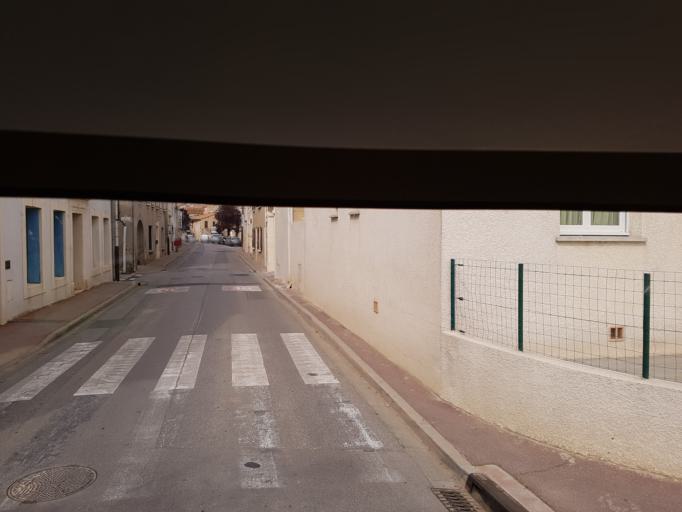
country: FR
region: Languedoc-Roussillon
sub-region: Departement de l'Aude
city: Fleury
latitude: 43.2276
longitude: 3.1339
